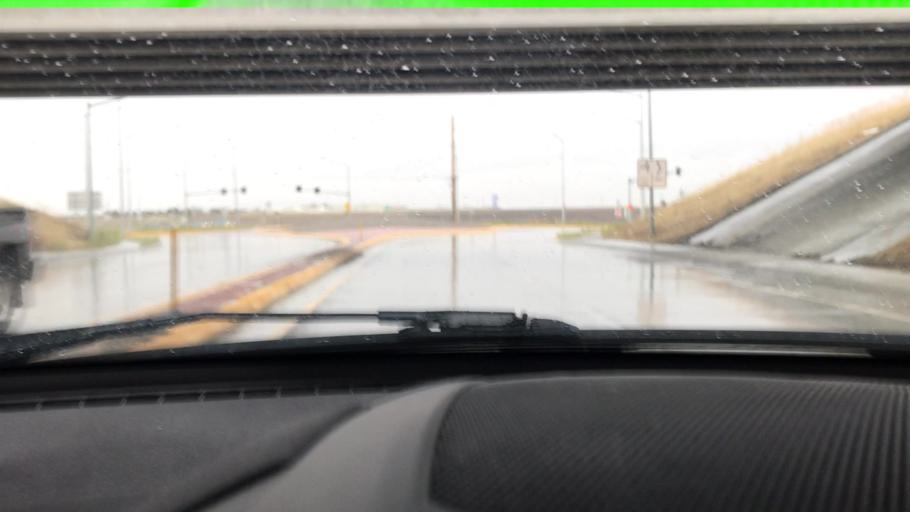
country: US
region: Montana
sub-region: Gallatin County
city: Belgrade
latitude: 45.7604
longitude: -111.1628
